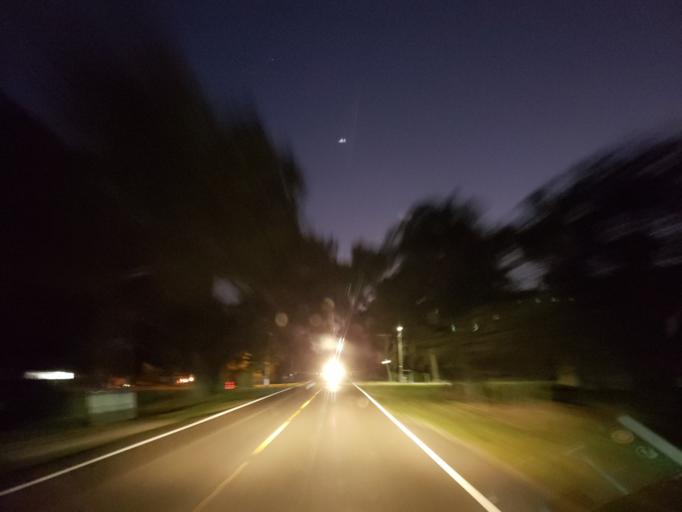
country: US
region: Florida
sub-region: Hillsborough County
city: Dover
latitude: 27.9768
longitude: -82.2198
